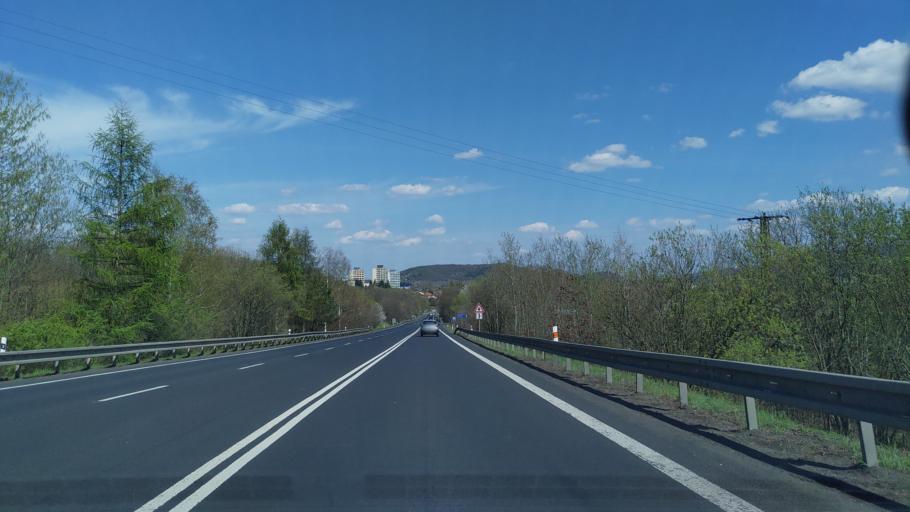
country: CZ
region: Ustecky
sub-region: Okres Chomutov
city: Klasterec nad Ohri
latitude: 50.3865
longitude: 13.1601
